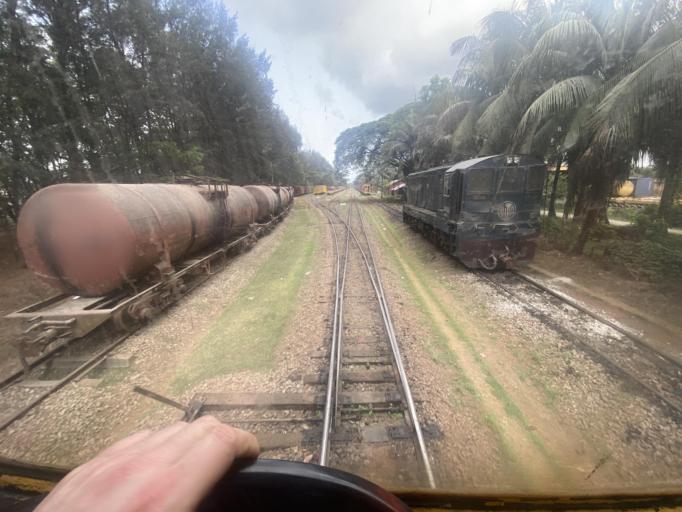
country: BD
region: Chittagong
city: Chittagong
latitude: 22.3204
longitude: 91.7838
